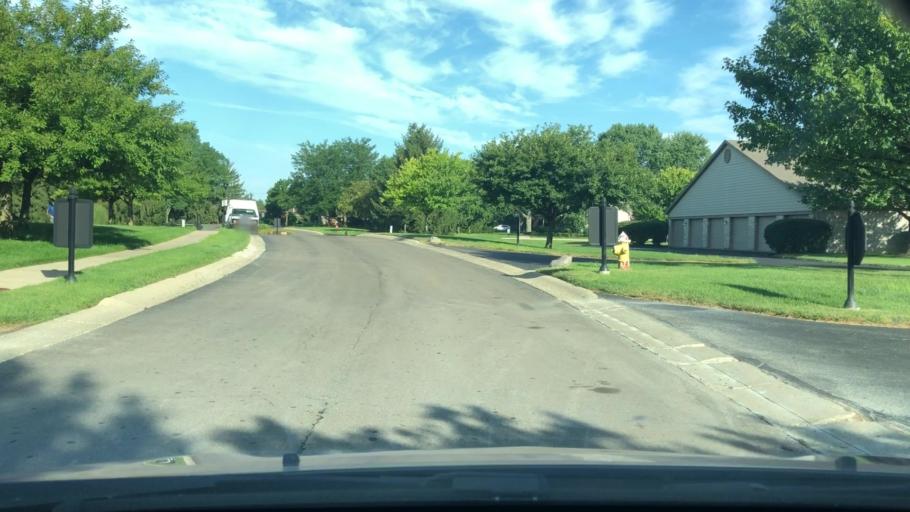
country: US
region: Ohio
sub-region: Montgomery County
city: Centerville
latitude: 39.6562
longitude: -84.1251
